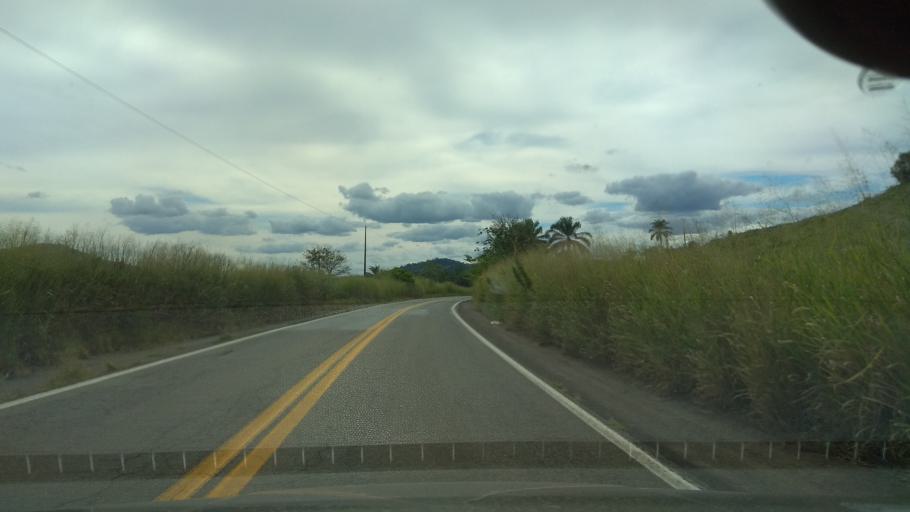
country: BR
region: Bahia
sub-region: Ipiau
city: Ipiau
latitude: -14.1880
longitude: -39.6592
